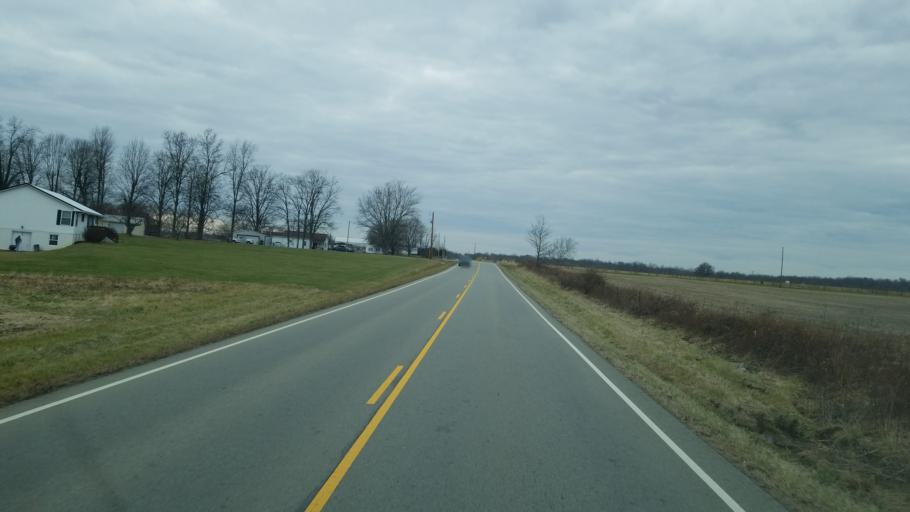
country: US
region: Ohio
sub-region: Highland County
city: Hillsboro
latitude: 39.2164
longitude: -83.4622
